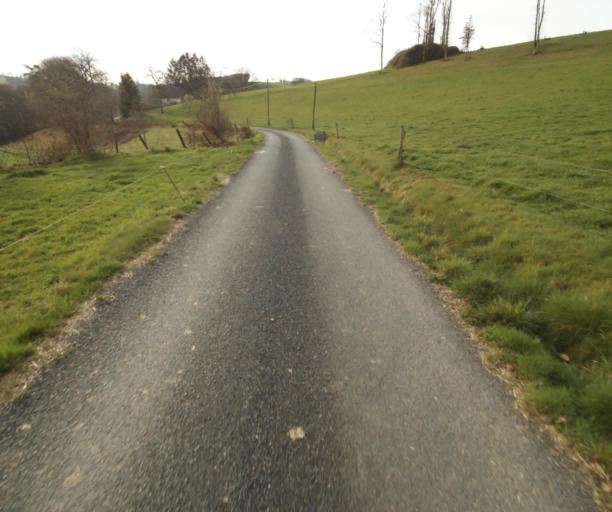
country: FR
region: Limousin
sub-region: Departement de la Correze
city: Chamboulive
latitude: 45.4581
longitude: 1.7580
